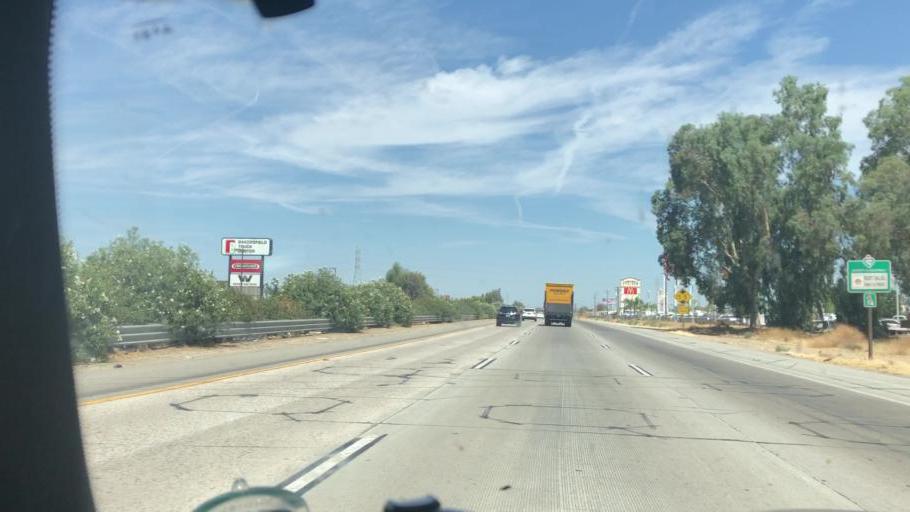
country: US
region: California
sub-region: Kern County
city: Oildale
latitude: 35.4350
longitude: -119.0762
